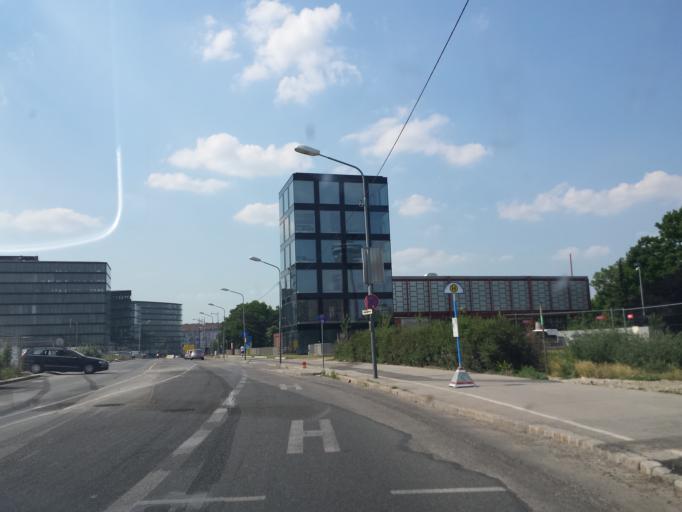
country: AT
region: Vienna
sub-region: Wien Stadt
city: Vienna
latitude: 48.1847
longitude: 16.3843
